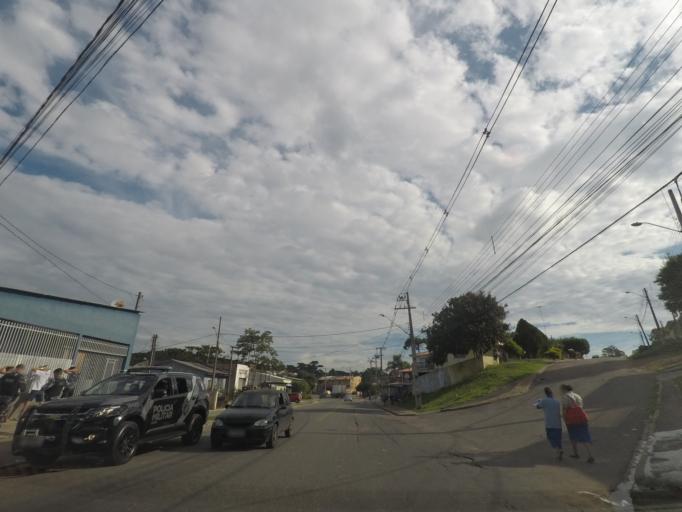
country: BR
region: Parana
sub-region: Sao Jose Dos Pinhais
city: Sao Jose dos Pinhais
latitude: -25.5534
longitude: -49.2930
